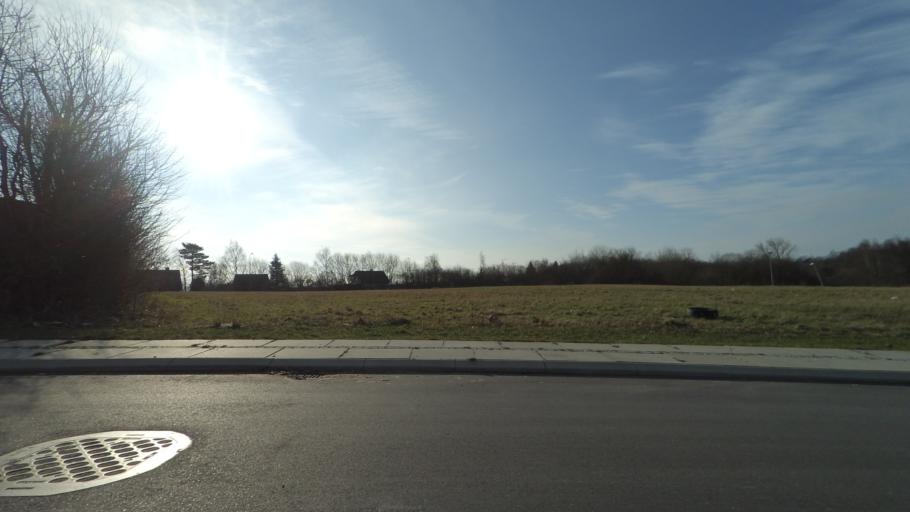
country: DK
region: Central Jutland
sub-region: Arhus Kommune
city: Tranbjerg
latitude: 56.1080
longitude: 10.1089
